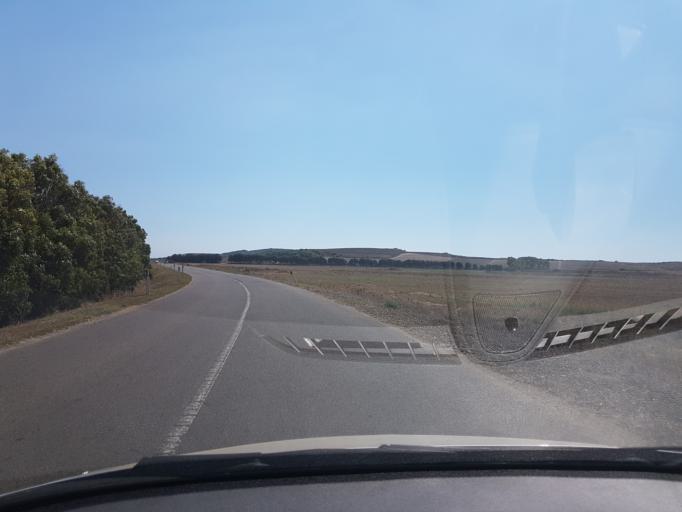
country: IT
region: Sardinia
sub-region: Provincia di Oristano
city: Nurachi
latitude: 39.9740
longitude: 8.4524
